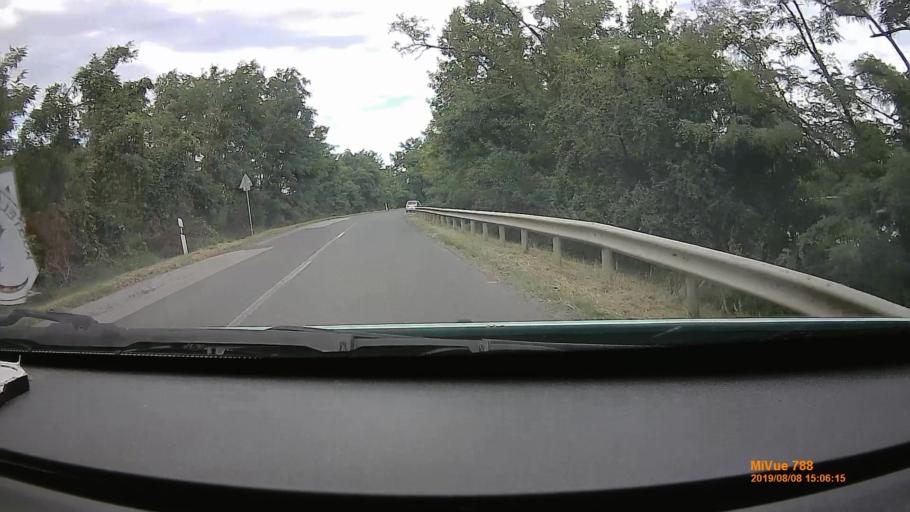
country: HU
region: Szabolcs-Szatmar-Bereg
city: Tunyogmatolcs
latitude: 47.9477
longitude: 22.4282
